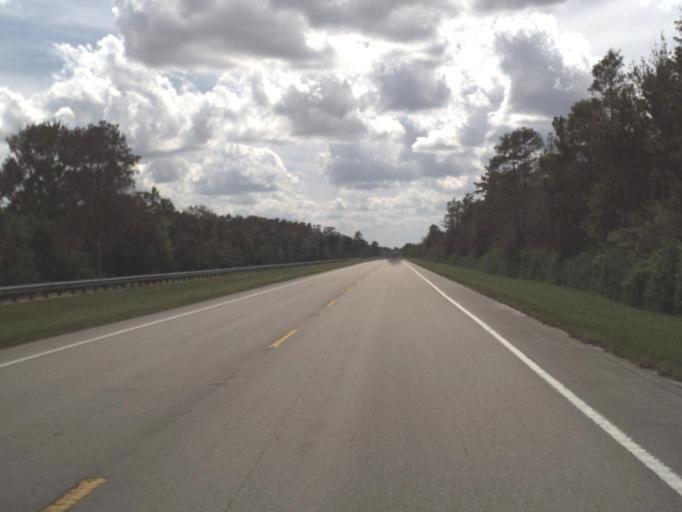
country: US
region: Florida
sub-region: Collier County
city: Orangetree
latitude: 26.0733
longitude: -81.3446
